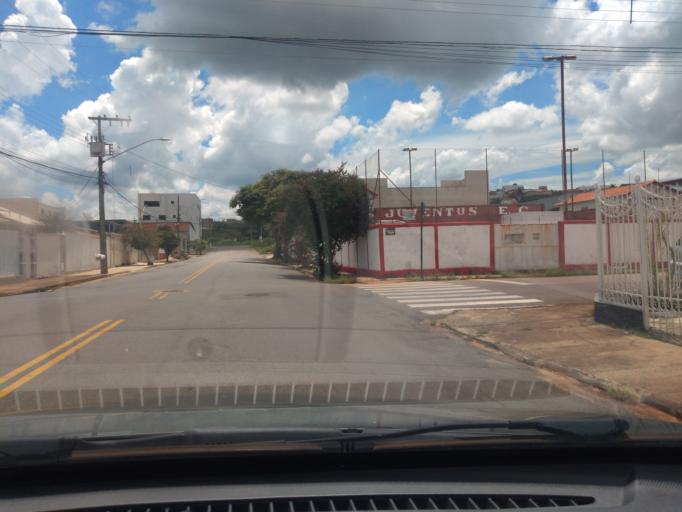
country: BR
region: Minas Gerais
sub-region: Tres Coracoes
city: Tres Coracoes
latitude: -21.6747
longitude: -45.2684
